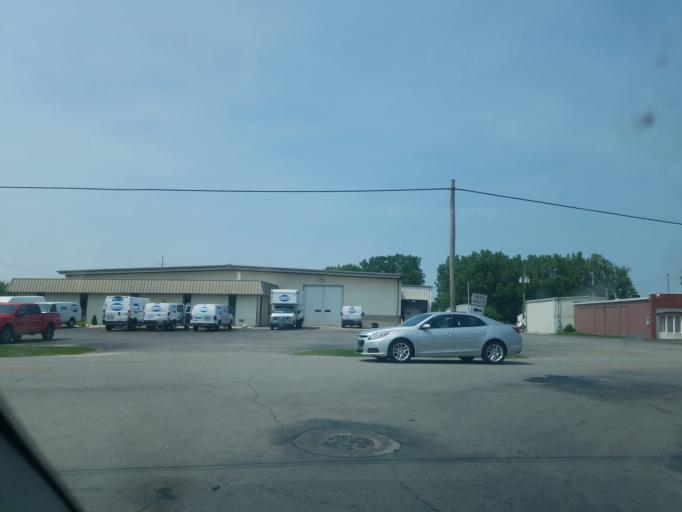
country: US
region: Ohio
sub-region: Seneca County
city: Tiffin
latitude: 41.1168
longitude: -83.2016
